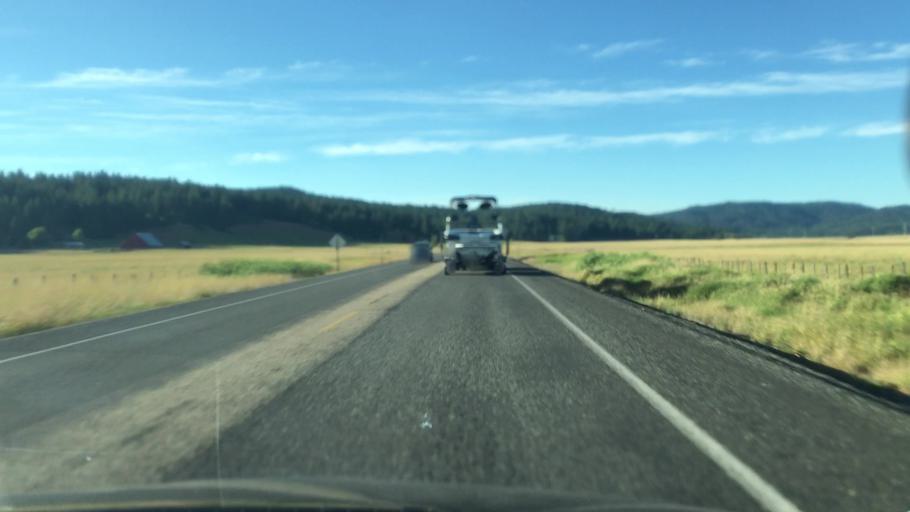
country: US
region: Idaho
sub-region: Valley County
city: Cascade
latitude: 44.5465
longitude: -116.0269
